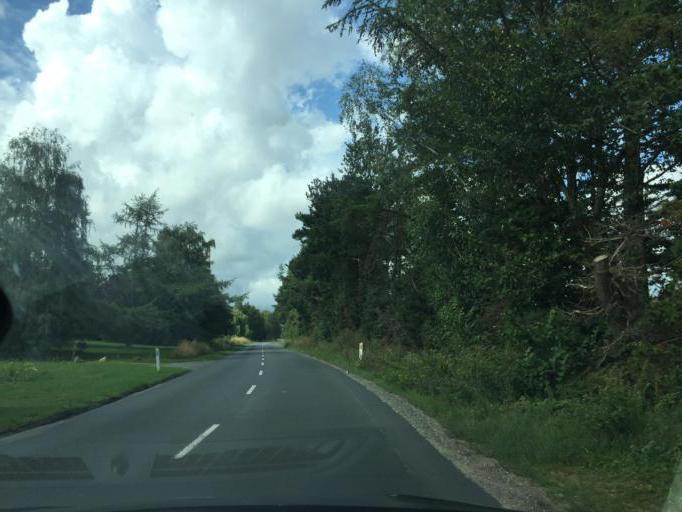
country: DK
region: South Denmark
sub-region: Odense Kommune
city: Stige
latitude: 55.4491
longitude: 10.3856
